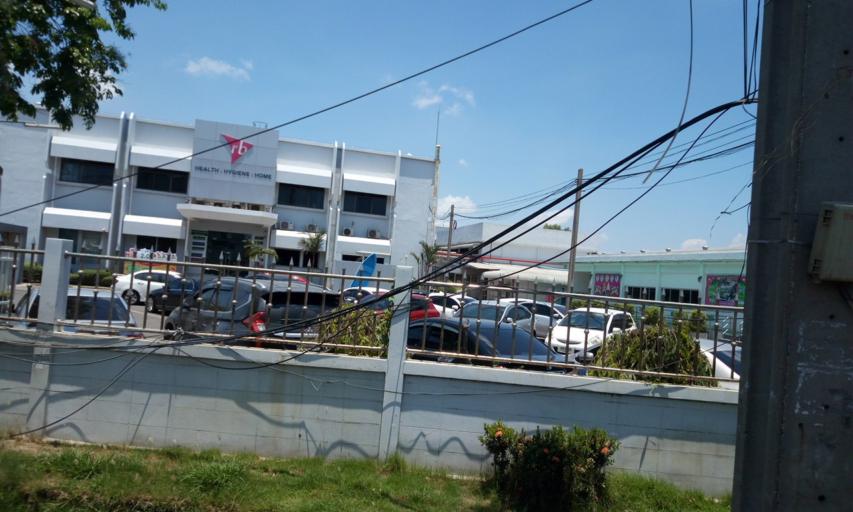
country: TH
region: Bangkok
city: Bang Na
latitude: 13.6236
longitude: 100.7059
